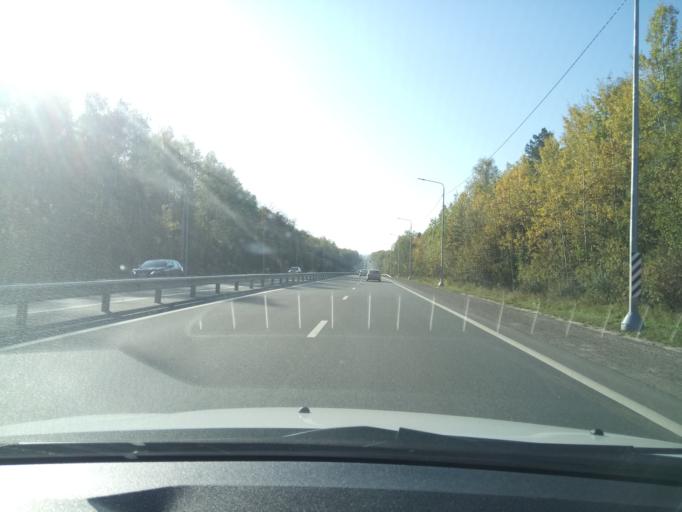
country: RU
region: Nizjnij Novgorod
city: Burevestnik
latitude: 56.0315
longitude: 43.9615
